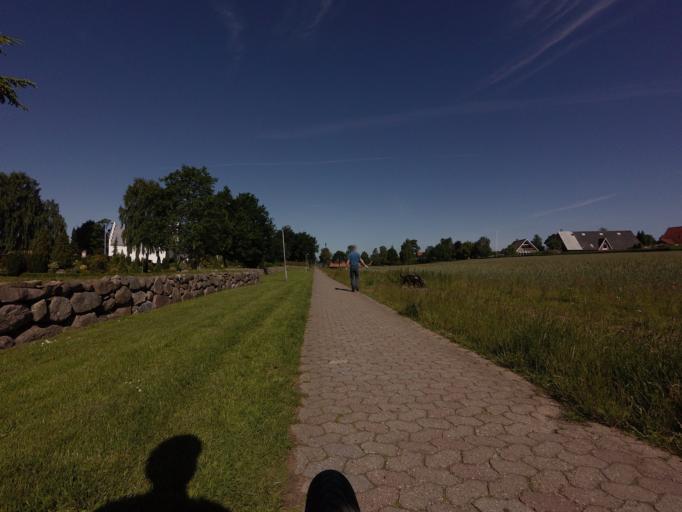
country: DK
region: Central Jutland
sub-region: Skanderborg Kommune
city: Ry
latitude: 55.9666
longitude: 9.7534
